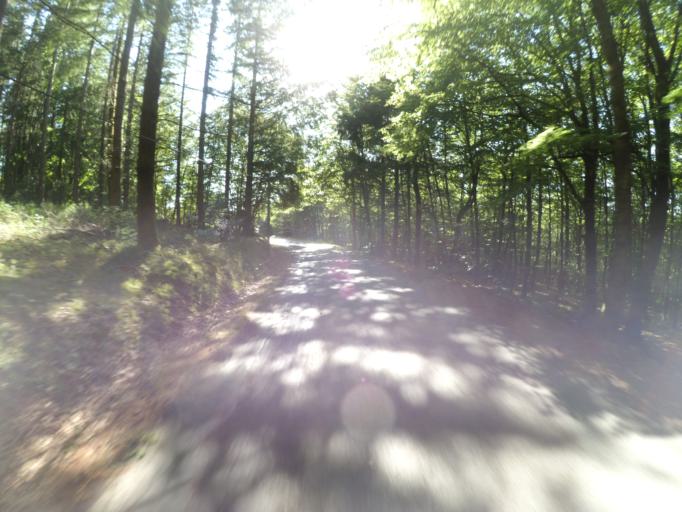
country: FR
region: Limousin
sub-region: Departement de la Correze
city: Bugeat
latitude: 45.6886
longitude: 1.9642
